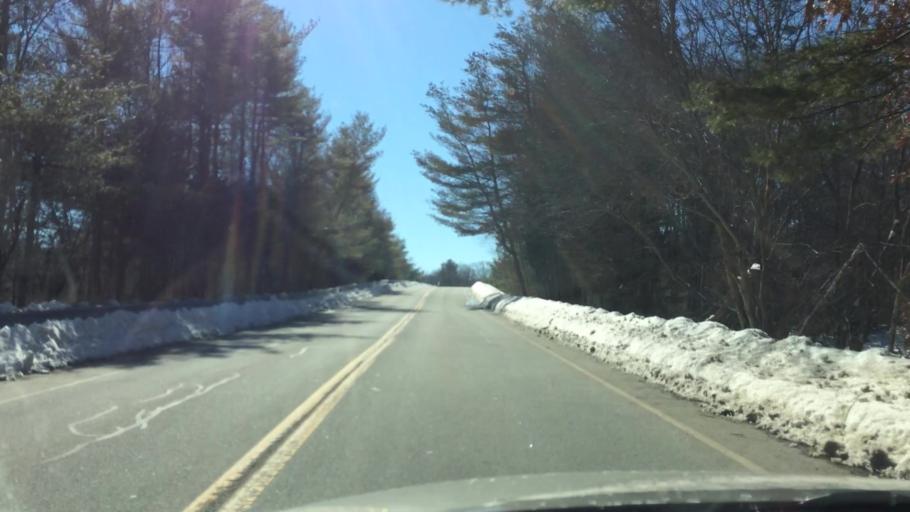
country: US
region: Massachusetts
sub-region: Middlesex County
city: Pinehurst
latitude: 42.5201
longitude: -71.2588
